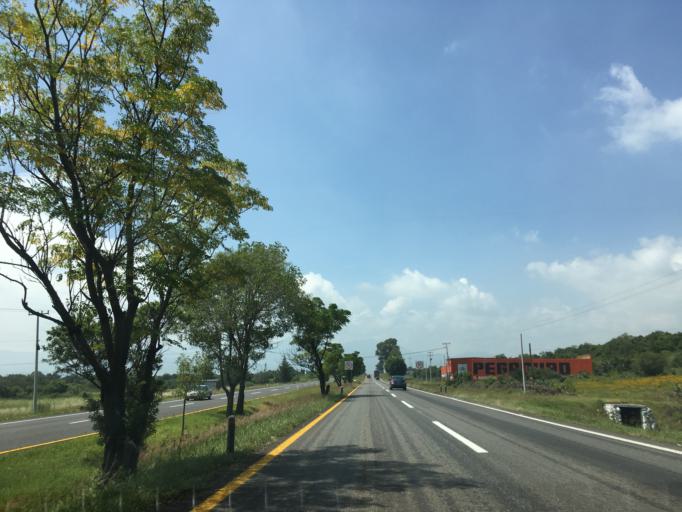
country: MX
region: Michoacan
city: Acuitzio del Canje
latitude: 19.5723
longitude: -101.3182
